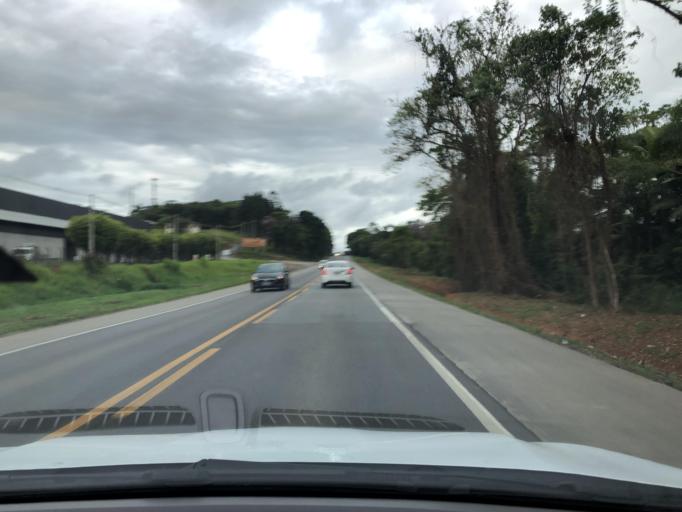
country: BR
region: Santa Catarina
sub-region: Joinville
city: Joinville
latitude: -26.4236
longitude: -48.7838
